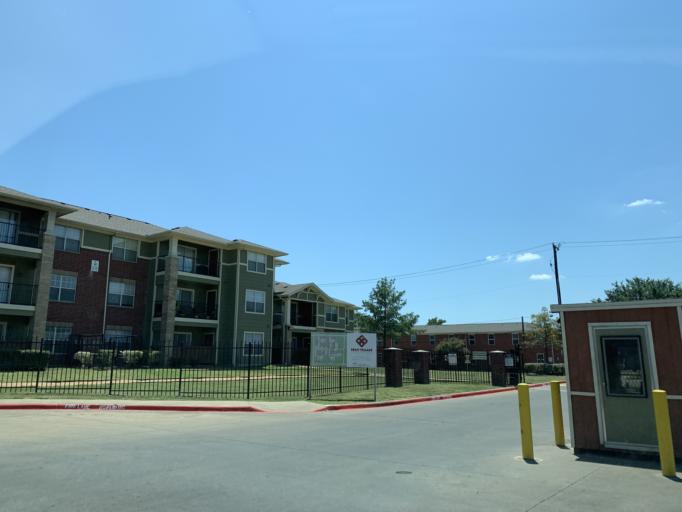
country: US
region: Texas
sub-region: Dallas County
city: Dallas
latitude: 32.7735
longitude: -96.7676
